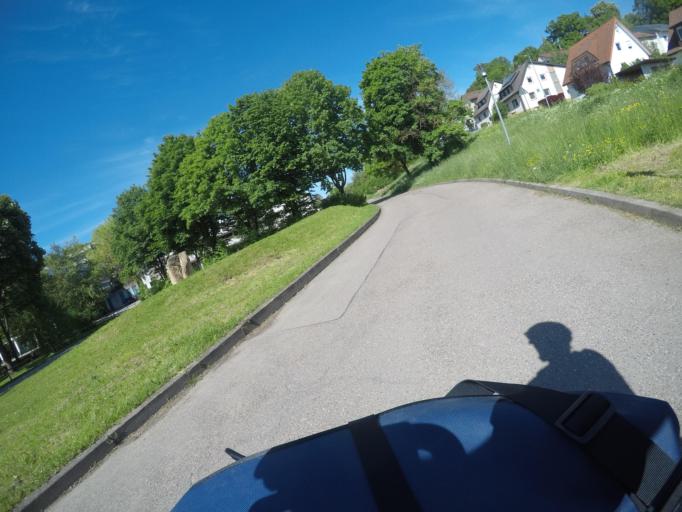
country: DE
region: Baden-Wuerttemberg
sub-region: Regierungsbezirk Stuttgart
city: Huttlingen
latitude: 48.8704
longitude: 10.0987
